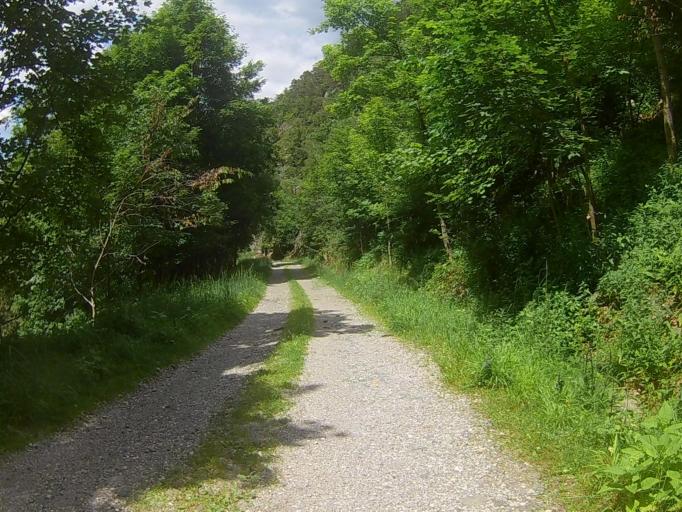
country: SI
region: Selnica ob Dravi
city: Selnica ob Dravi
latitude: 46.5140
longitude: 15.4652
